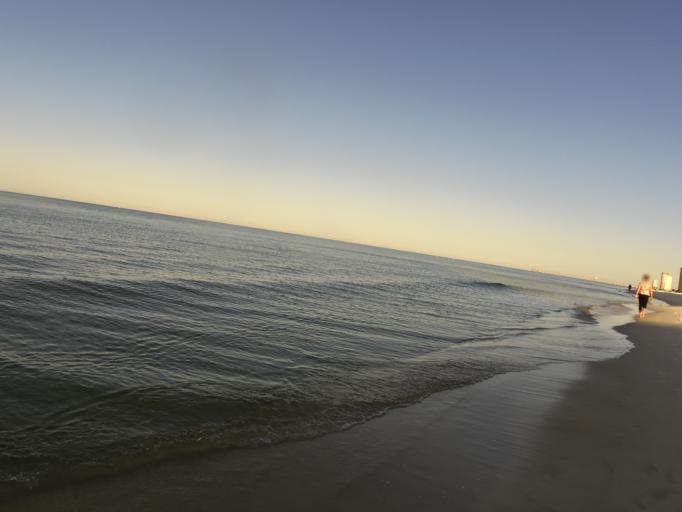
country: US
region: Florida
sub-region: Bay County
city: Panama City Beach
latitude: 30.2065
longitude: -85.8619
